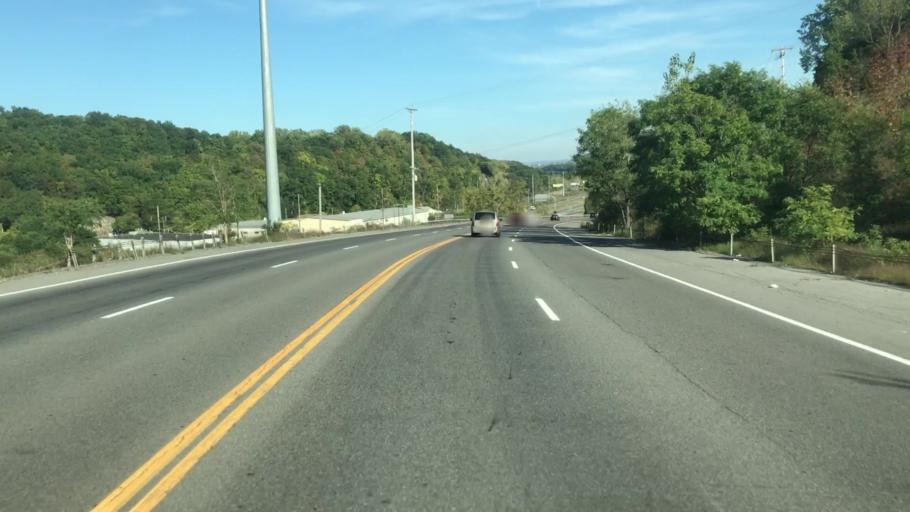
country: US
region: New York
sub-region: Onondaga County
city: Nedrow
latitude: 43.0070
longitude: -76.1260
